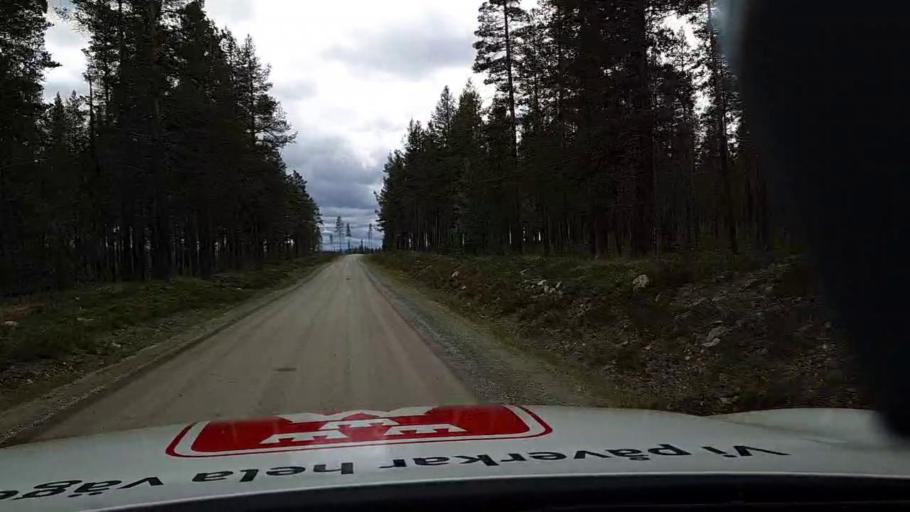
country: SE
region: Jaemtland
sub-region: Are Kommun
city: Jarpen
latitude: 62.8156
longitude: 13.8094
